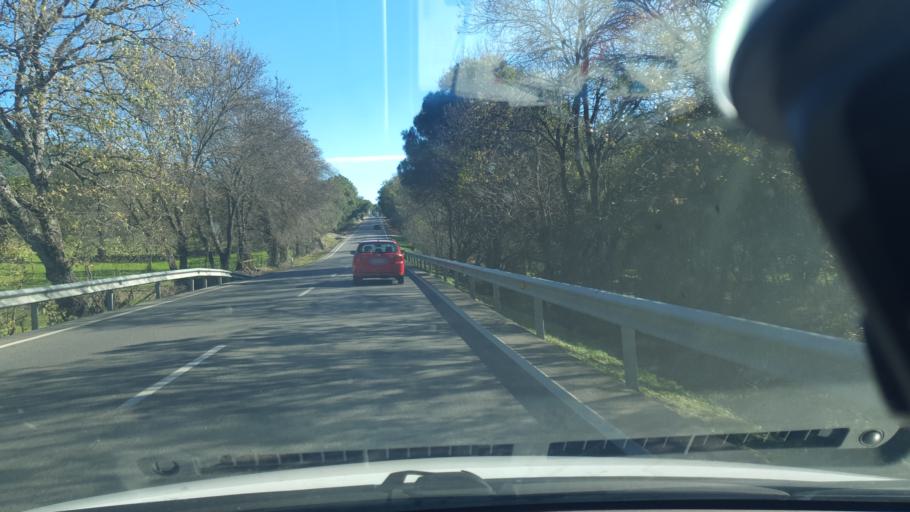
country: ES
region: Castille and Leon
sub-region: Provincia de Avila
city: Piedralaves
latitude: 40.3139
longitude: -4.6687
